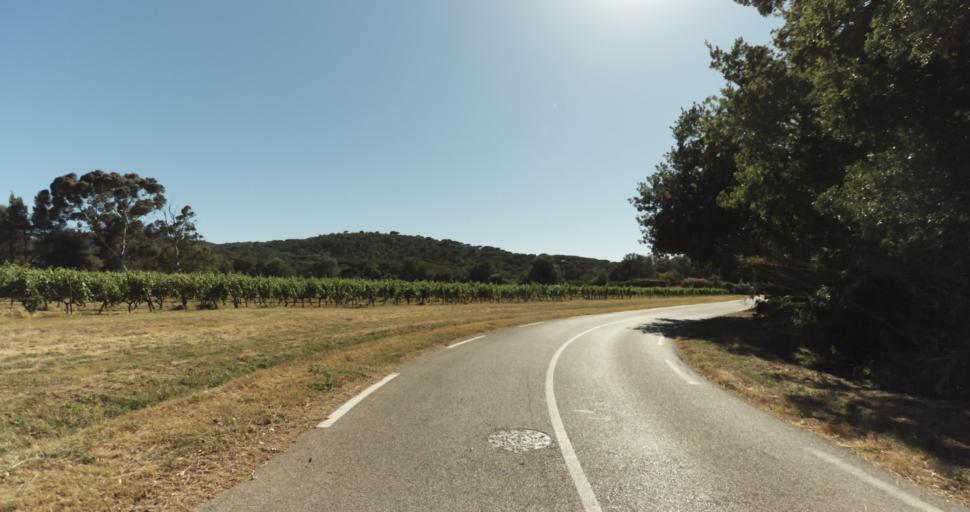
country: FR
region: Provence-Alpes-Cote d'Azur
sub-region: Departement du Var
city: Gassin
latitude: 43.2527
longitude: 6.5945
